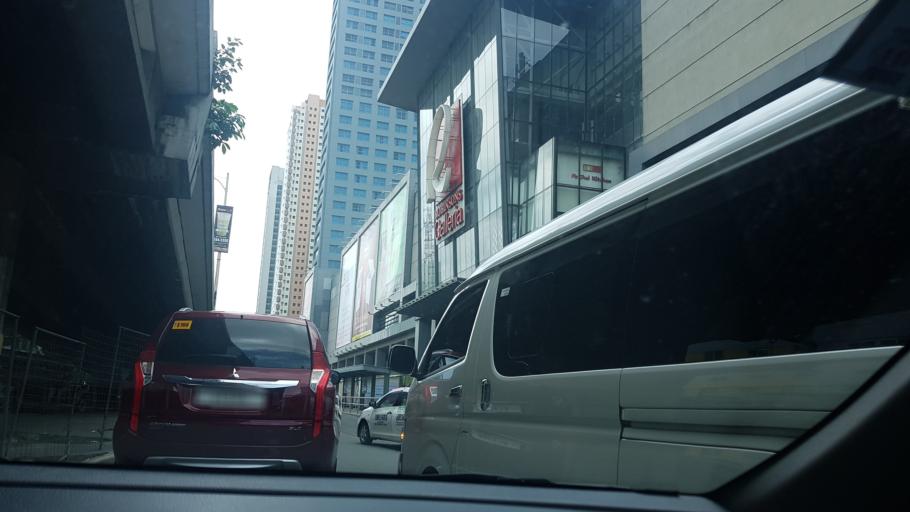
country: PH
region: Metro Manila
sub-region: Pasig
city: Pasig City
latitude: 14.5920
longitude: 121.0598
